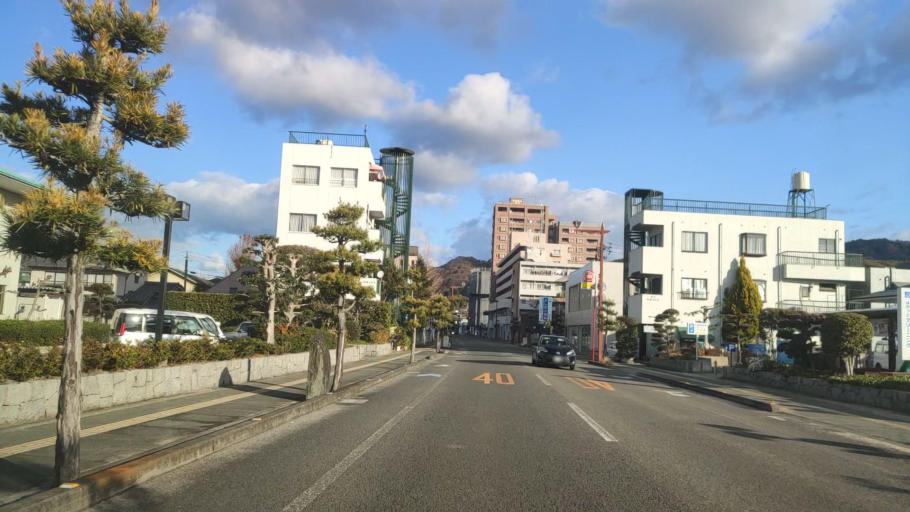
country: JP
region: Ehime
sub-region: Shikoku-chuo Shi
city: Matsuyama
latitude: 33.8501
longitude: 132.7808
